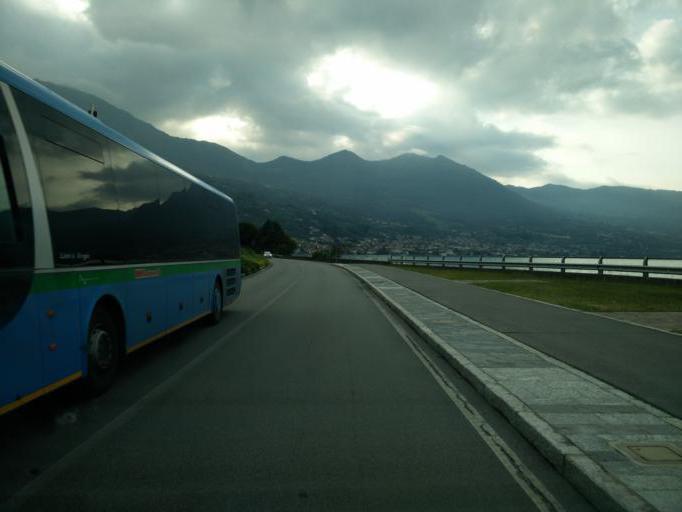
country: IT
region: Lombardy
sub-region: Provincia di Brescia
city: Marone
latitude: 45.7276
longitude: 10.0971
